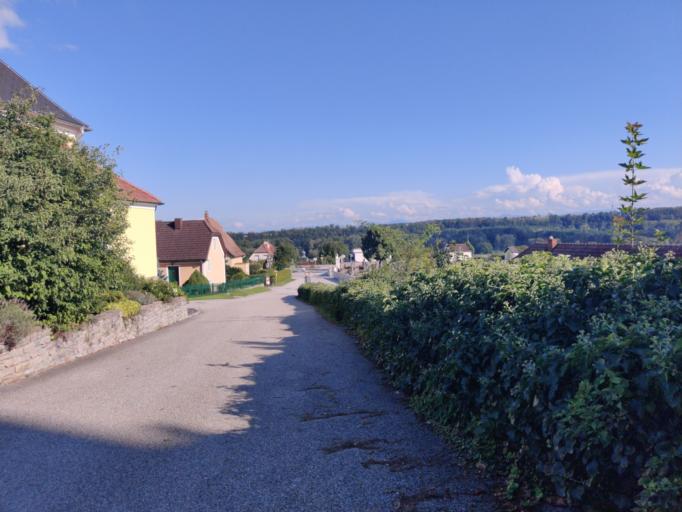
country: AT
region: Lower Austria
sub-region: Politischer Bezirk Melk
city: Emmersdorf an der Donau
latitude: 48.2429
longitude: 15.3346
